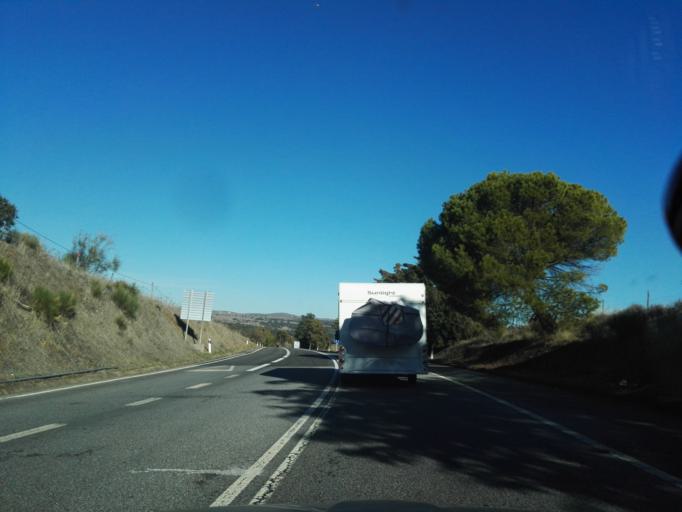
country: PT
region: Evora
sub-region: Vila Vicosa
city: Vila Vicosa
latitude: 38.8493
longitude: -7.3378
